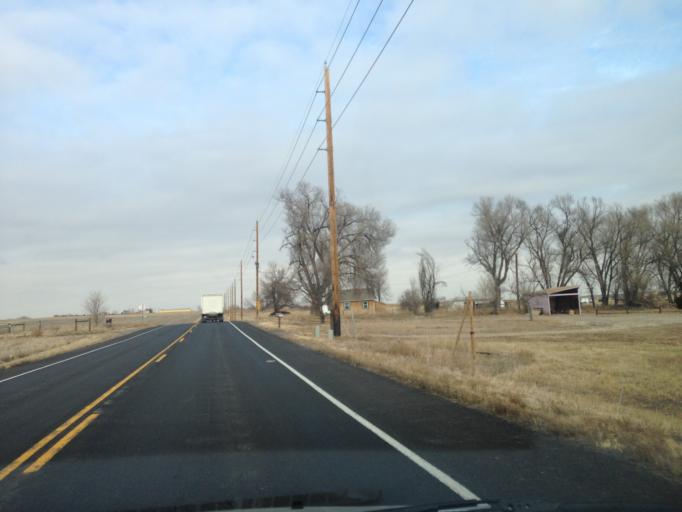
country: US
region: Colorado
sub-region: Boulder County
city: Lafayette
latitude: 40.0067
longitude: -105.0745
